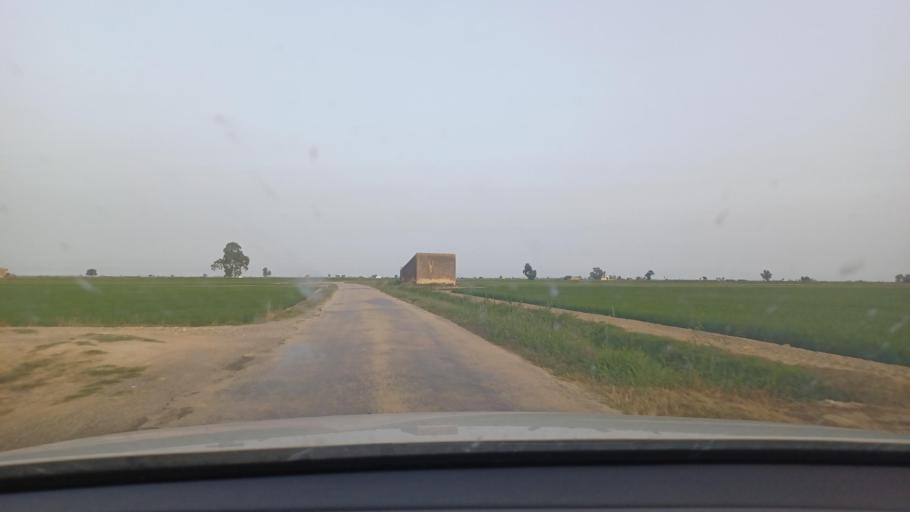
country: ES
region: Catalonia
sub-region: Provincia de Tarragona
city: Deltebre
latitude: 40.6967
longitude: 0.6479
